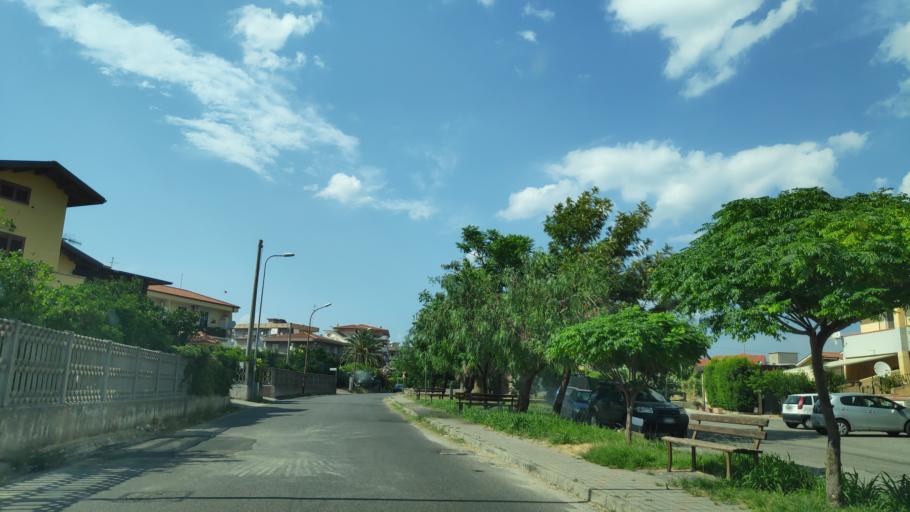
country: IT
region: Calabria
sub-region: Provincia di Catanzaro
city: Marina di Davoli
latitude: 38.6647
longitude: 16.5423
